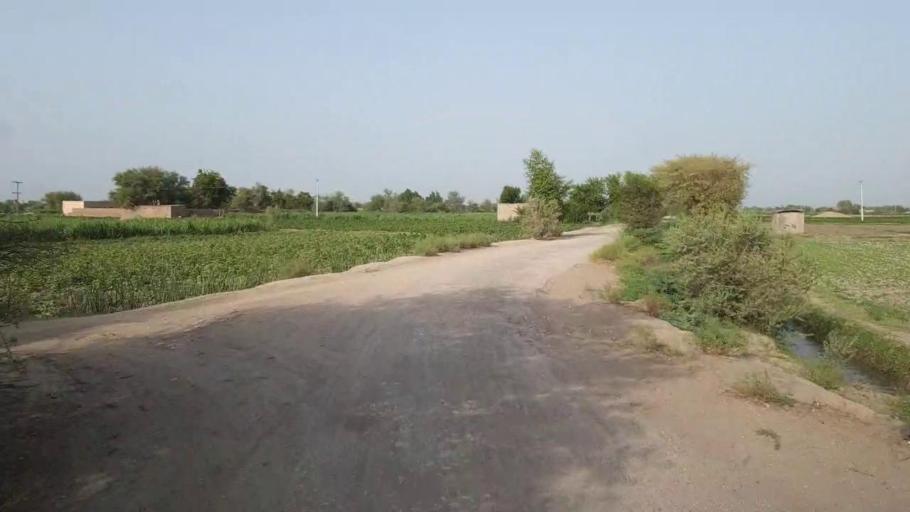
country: PK
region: Sindh
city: Daur
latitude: 26.3432
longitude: 68.2633
